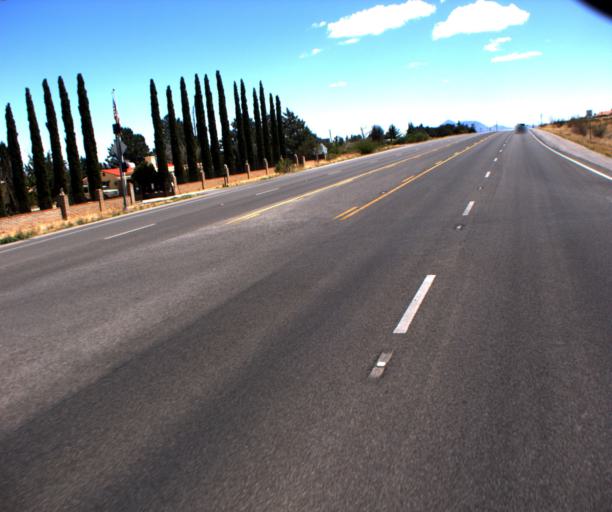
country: US
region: Arizona
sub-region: Cochise County
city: Sierra Vista Southeast
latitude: 31.4370
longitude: -110.2471
